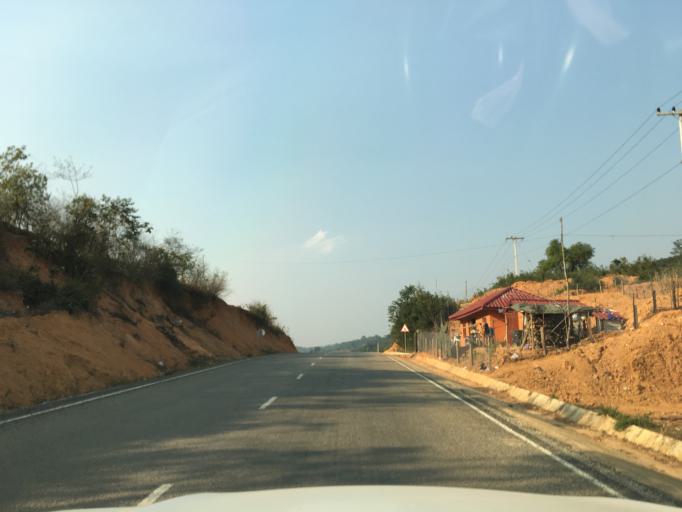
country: LA
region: Houaphan
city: Xam Nua
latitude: 20.5748
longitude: 104.0565
